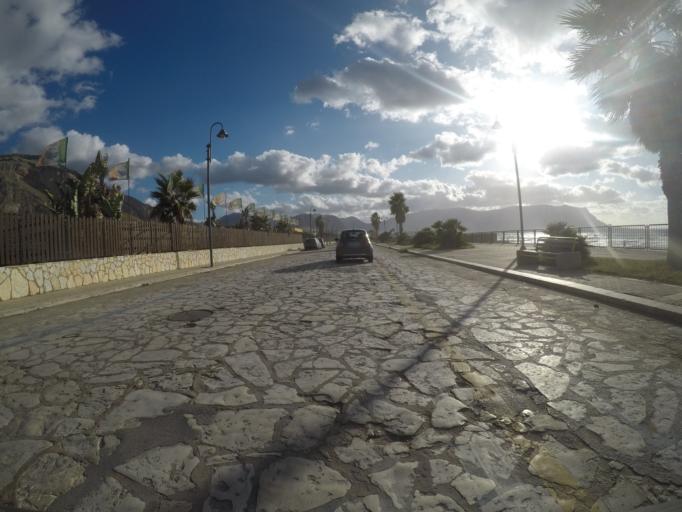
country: IT
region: Sicily
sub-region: Palermo
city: Isola delle Femmine
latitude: 38.1905
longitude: 13.2430
